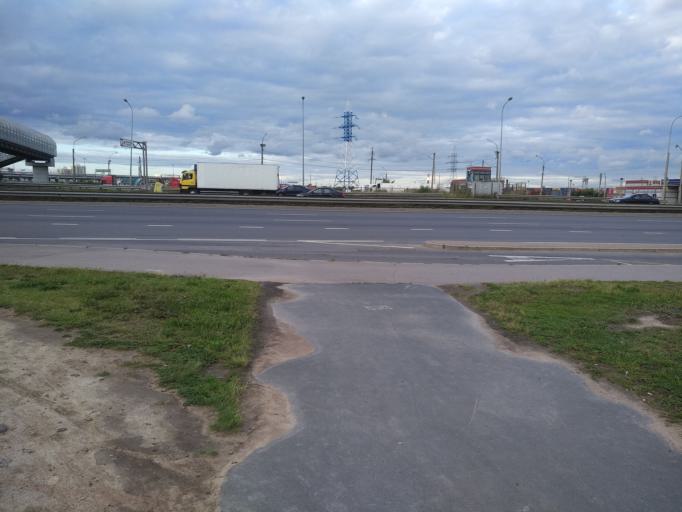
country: RU
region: St.-Petersburg
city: Shushary
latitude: 59.8117
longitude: 30.3806
